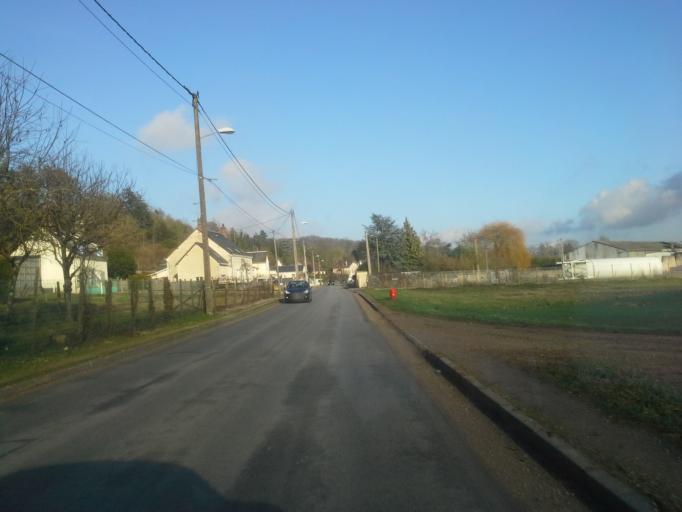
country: FR
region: Centre
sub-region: Departement du Loir-et-Cher
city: Naveil
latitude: 47.8017
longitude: 1.0300
